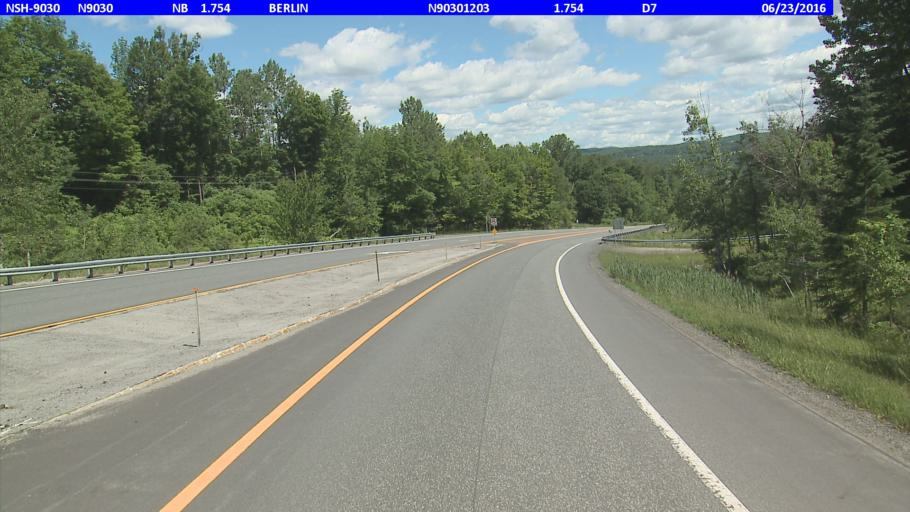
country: US
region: Vermont
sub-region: Washington County
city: Montpelier
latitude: 44.2253
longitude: -72.5578
